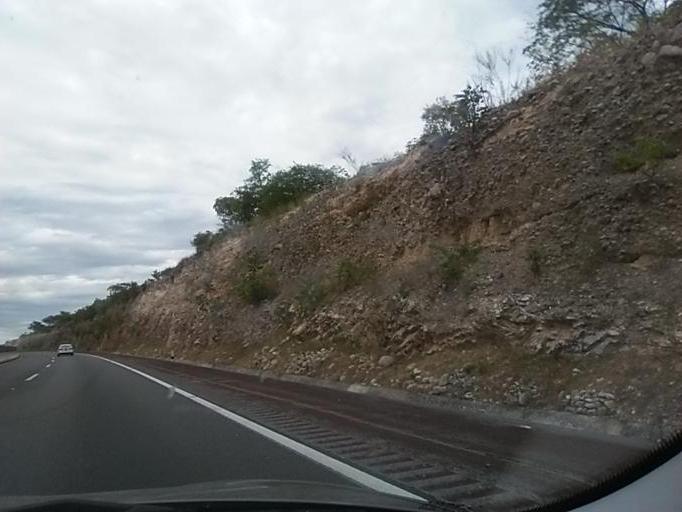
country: MX
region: Guerrero
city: Copalillo
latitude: 18.0928
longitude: -99.2209
